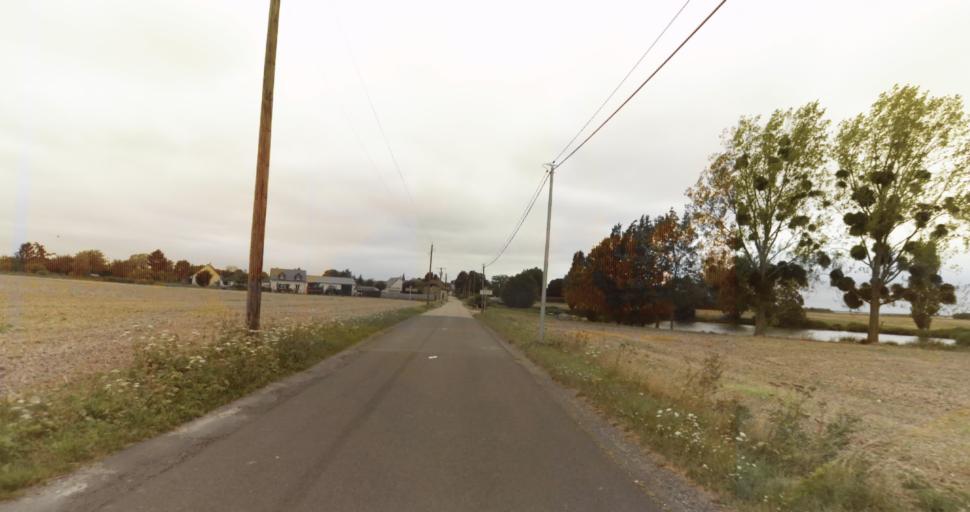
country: FR
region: Haute-Normandie
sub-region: Departement de l'Eure
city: La Couture-Boussey
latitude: 48.9052
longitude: 1.3525
